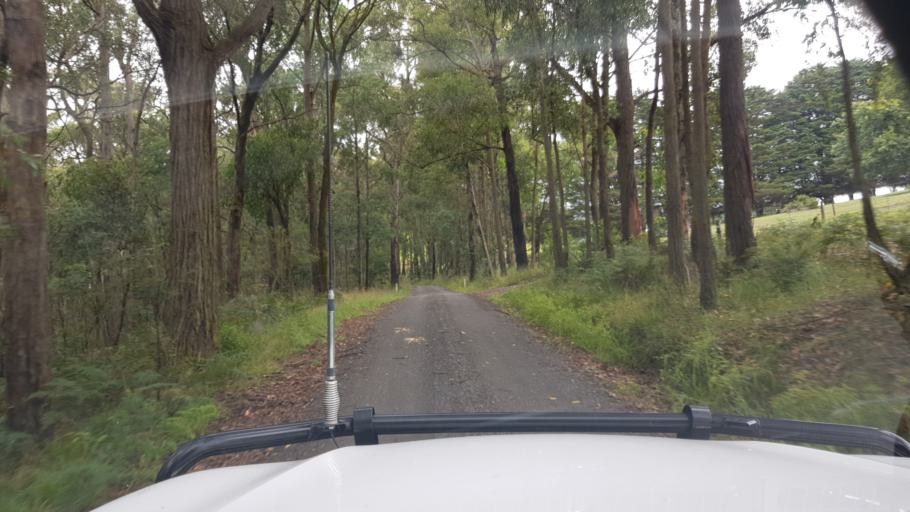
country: AU
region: Victoria
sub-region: Baw Baw
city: Warragul
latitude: -38.0599
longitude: 146.0153
